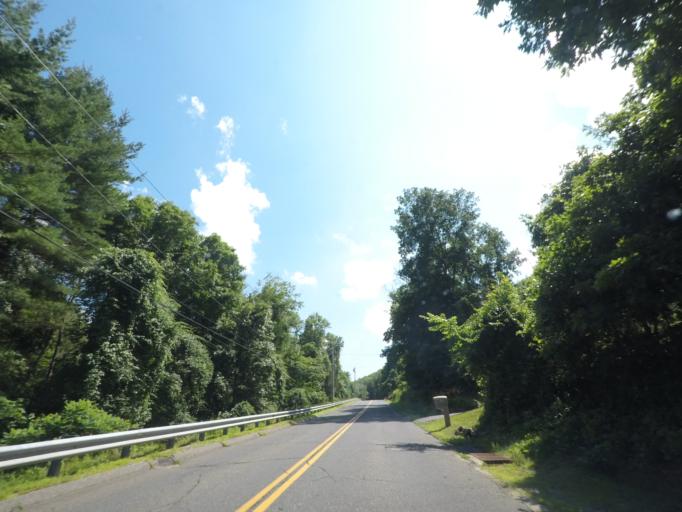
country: US
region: Massachusetts
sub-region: Hampden County
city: Palmer
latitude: 42.1372
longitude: -72.3332
